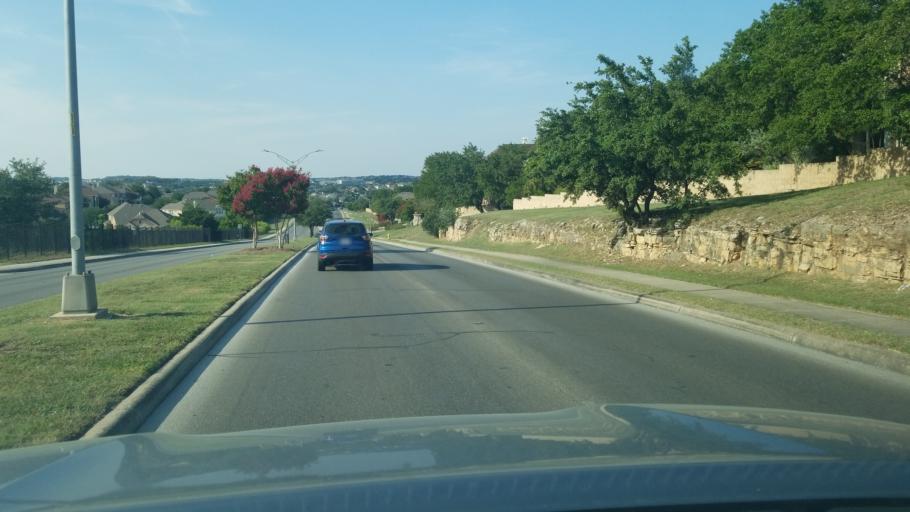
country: US
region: Texas
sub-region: Bexar County
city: Hollywood Park
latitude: 29.6424
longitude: -98.5066
